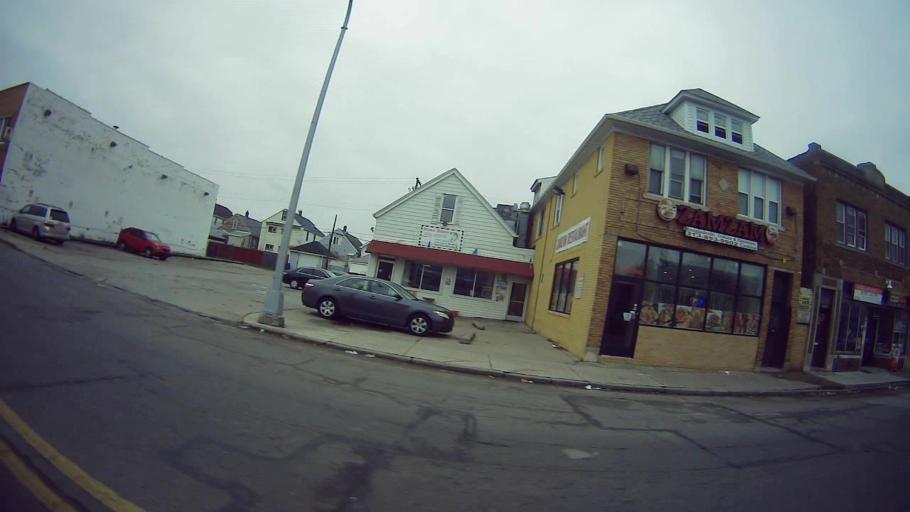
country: US
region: Michigan
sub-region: Wayne County
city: Hamtramck
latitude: 42.4063
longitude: -83.0552
